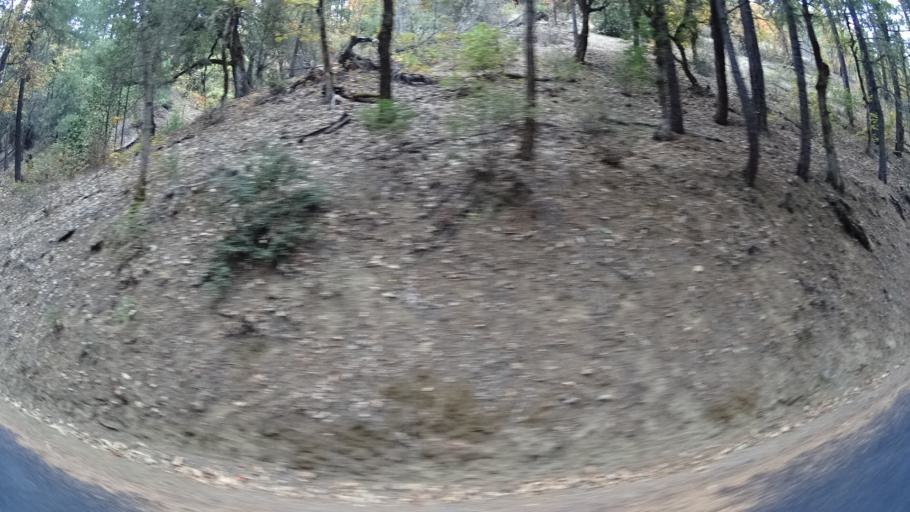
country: US
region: California
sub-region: Siskiyou County
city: Happy Camp
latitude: 41.8627
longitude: -123.1492
